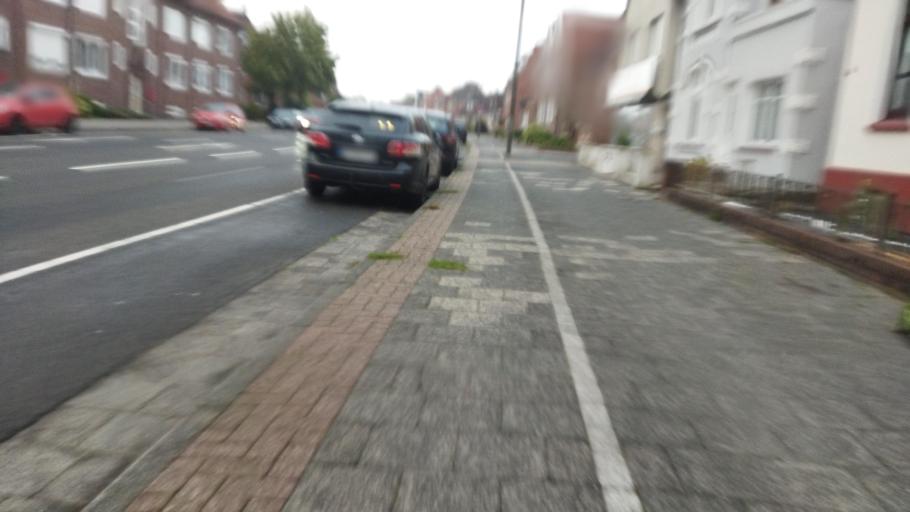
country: DE
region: Lower Saxony
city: Emden
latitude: 53.3787
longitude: 7.2062
